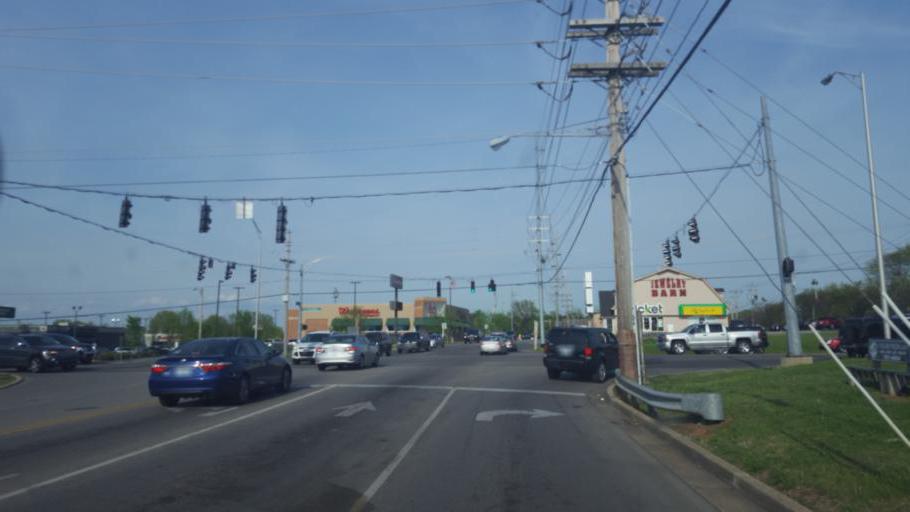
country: US
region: Kentucky
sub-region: Warren County
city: Bowling Green
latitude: 36.9458
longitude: -86.4237
